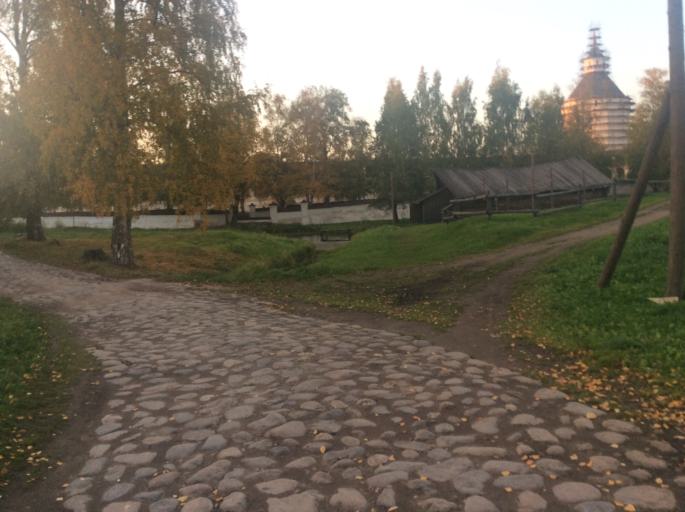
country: RU
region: Vologda
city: Kirillov
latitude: 59.8573
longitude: 38.3692
